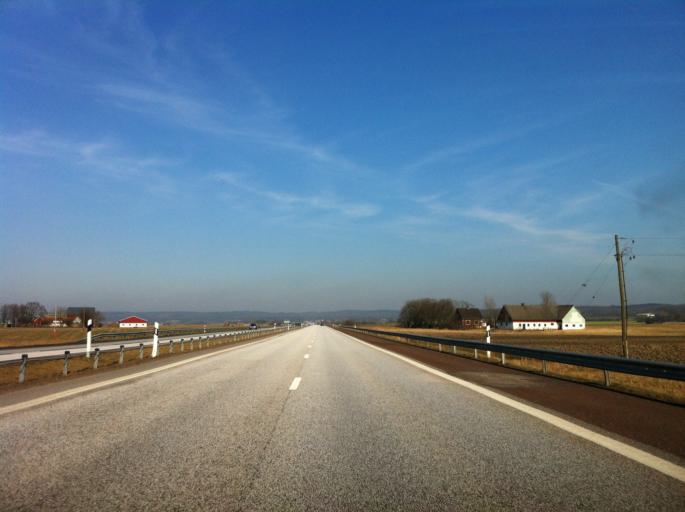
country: SE
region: Skane
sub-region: Angelholms Kommun
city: AEngelholm
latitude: 56.2795
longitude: 12.8974
